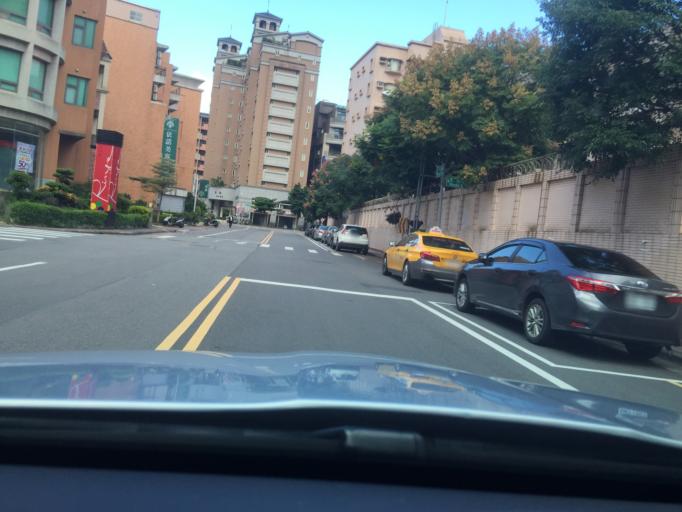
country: TW
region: Taiwan
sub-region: Hsinchu
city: Zhubei
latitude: 24.8294
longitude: 121.0163
